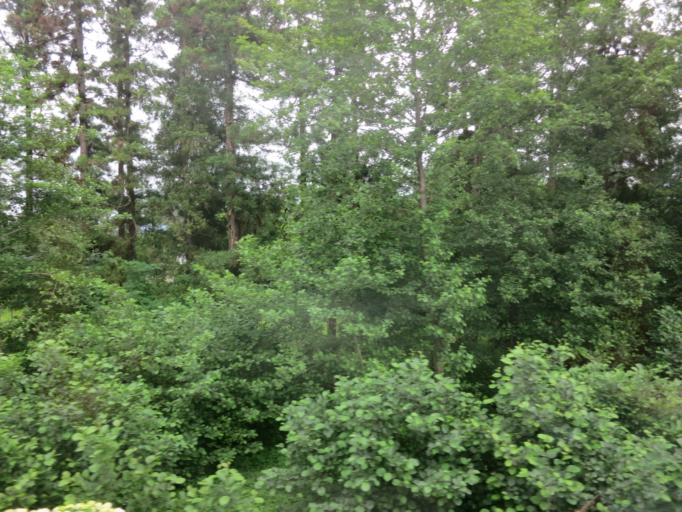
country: GE
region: Ajaria
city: Kobuleti
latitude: 41.8012
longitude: 41.7751
